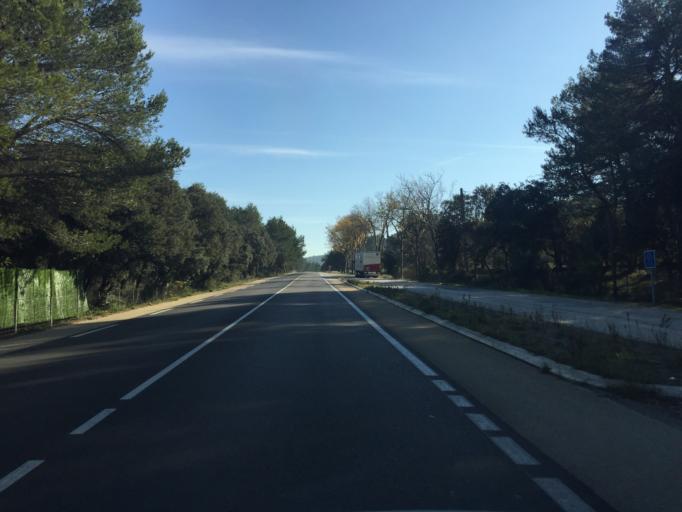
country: FR
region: Provence-Alpes-Cote d'Azur
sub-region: Departement du Vaucluse
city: Cavaillon
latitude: 43.8131
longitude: 5.0206
